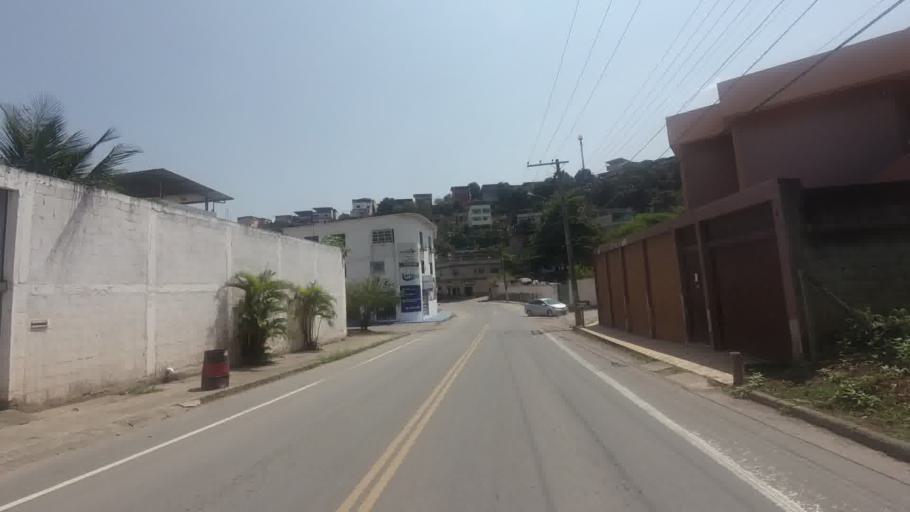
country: BR
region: Espirito Santo
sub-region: Cachoeiro De Itapemirim
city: Cachoeiro de Itapemirim
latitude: -20.8521
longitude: -41.0931
